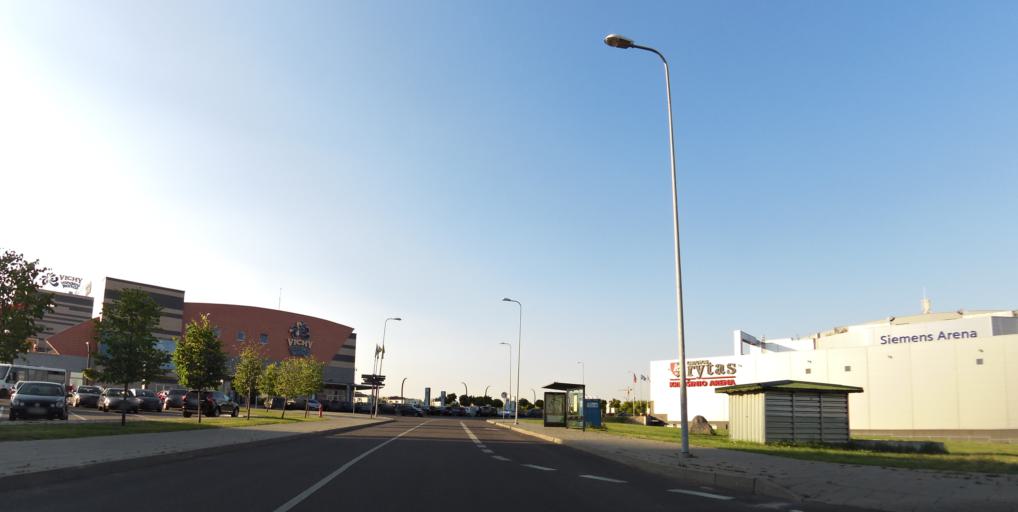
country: LT
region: Vilnius County
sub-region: Vilnius
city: Vilnius
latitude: 54.7152
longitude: 25.2778
